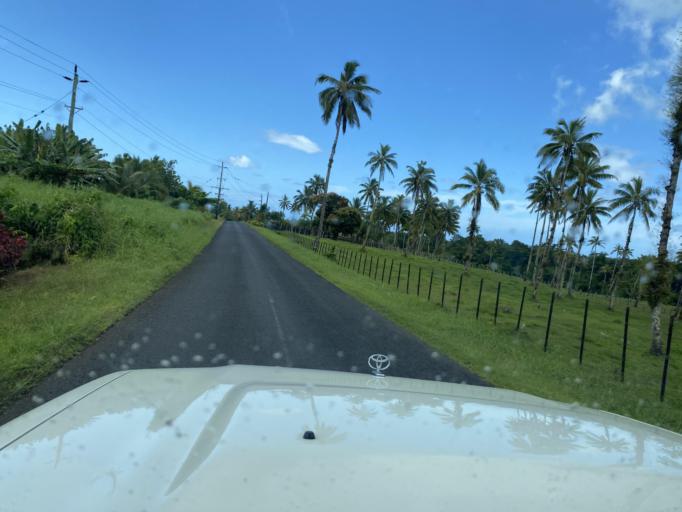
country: WS
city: Matavai
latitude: -13.9856
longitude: -171.5878
